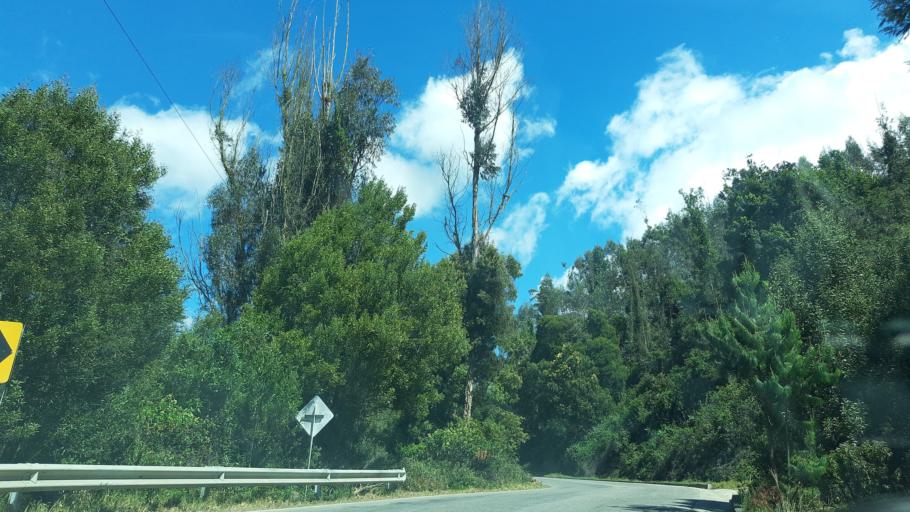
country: CO
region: Boyaca
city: Samaca
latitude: 5.4828
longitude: -73.4743
